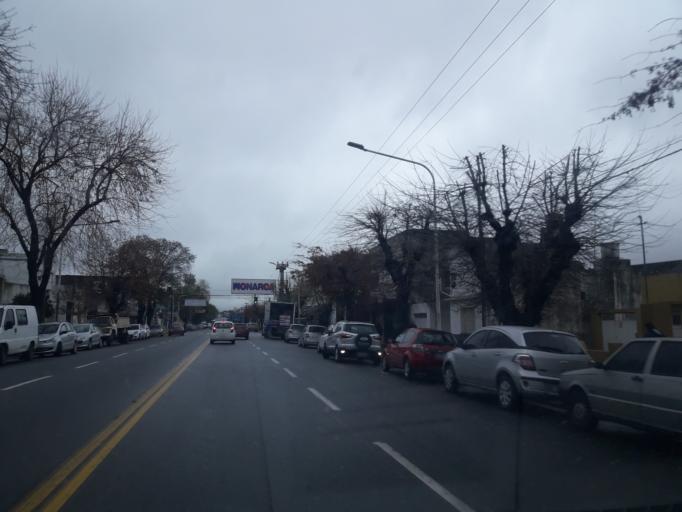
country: AR
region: Buenos Aires
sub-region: Partido de Tandil
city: Tandil
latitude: -37.3219
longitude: -59.1495
